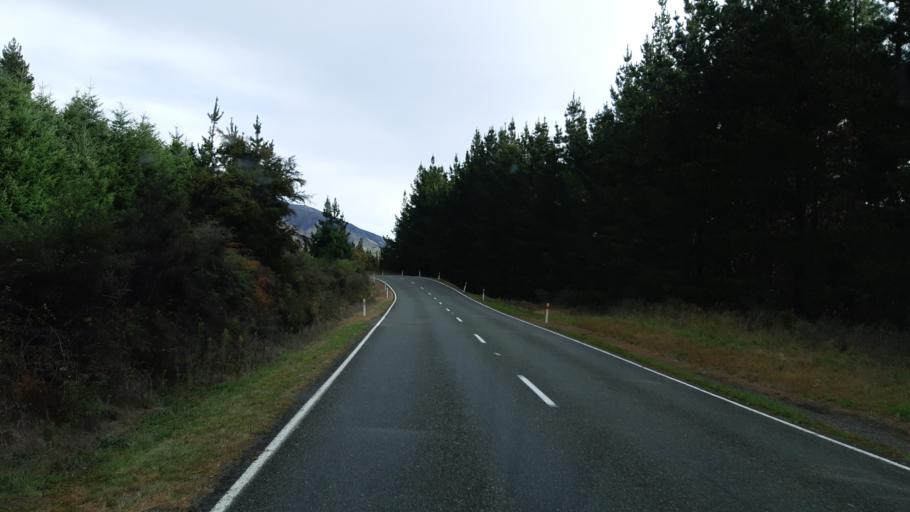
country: NZ
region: Tasman
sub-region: Tasman District
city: Wakefield
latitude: -41.7054
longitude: 173.1223
